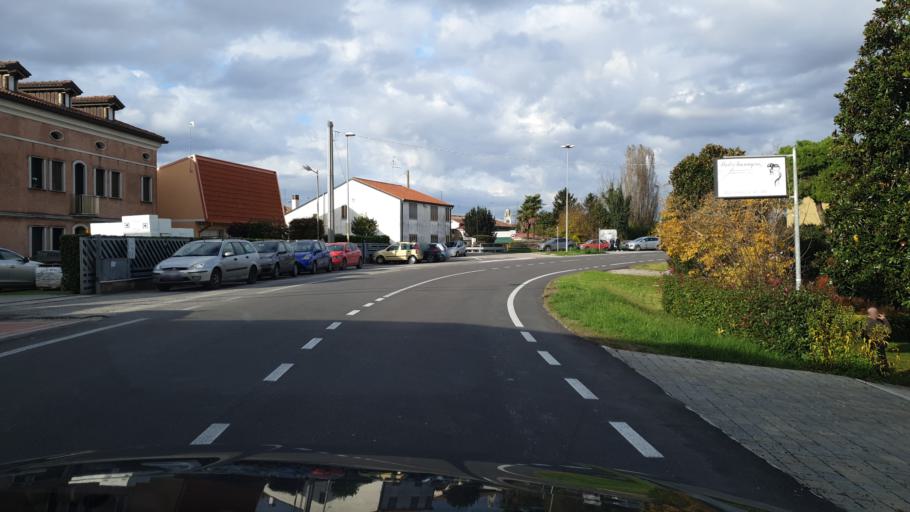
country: IT
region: Veneto
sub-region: Provincia di Rovigo
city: Villanova del Ghebbo Canton
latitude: 45.0508
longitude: 11.6449
